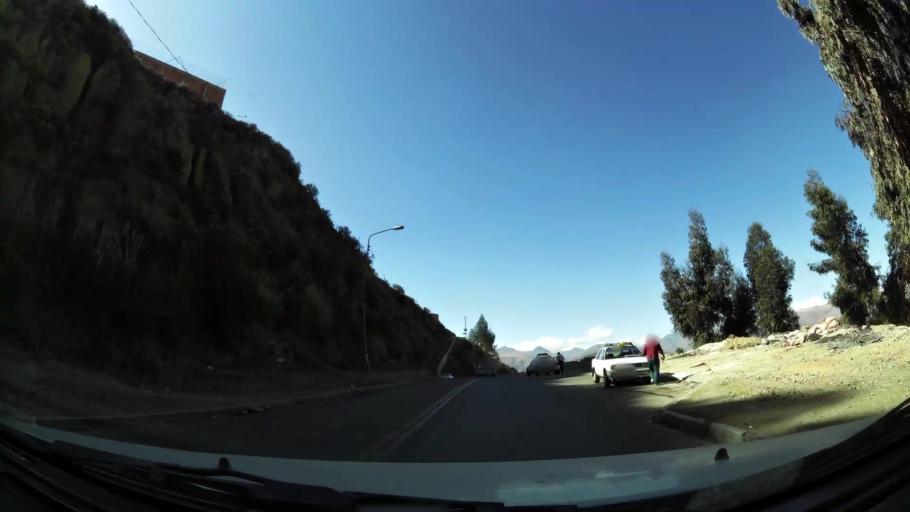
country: BO
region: La Paz
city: La Paz
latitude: -16.5180
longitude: -68.1472
